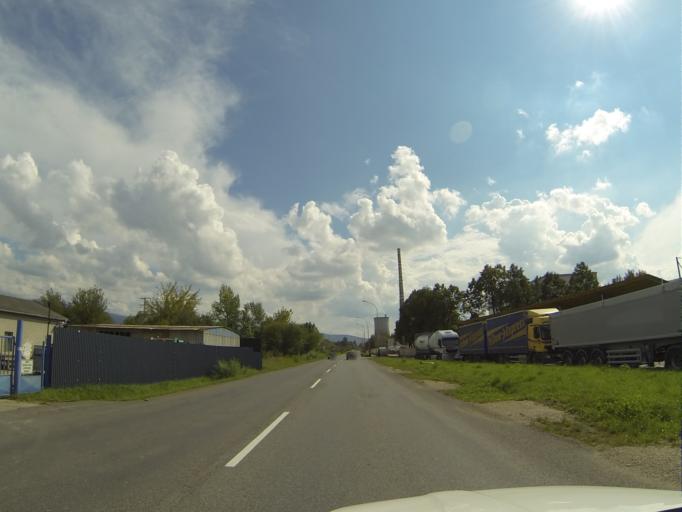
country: SK
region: Nitriansky
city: Novaky
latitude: 48.7092
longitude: 18.5373
